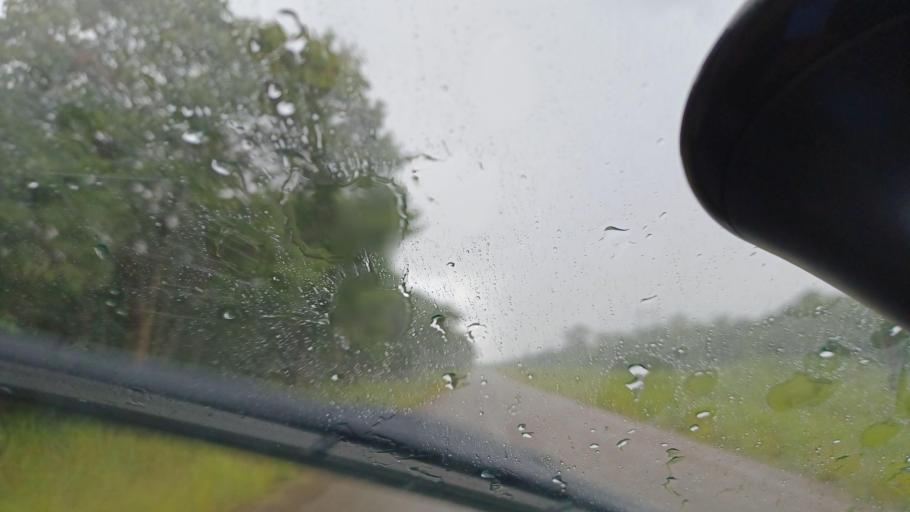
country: ZM
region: North-Western
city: Kasempa
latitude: -13.0910
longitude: 25.9402
